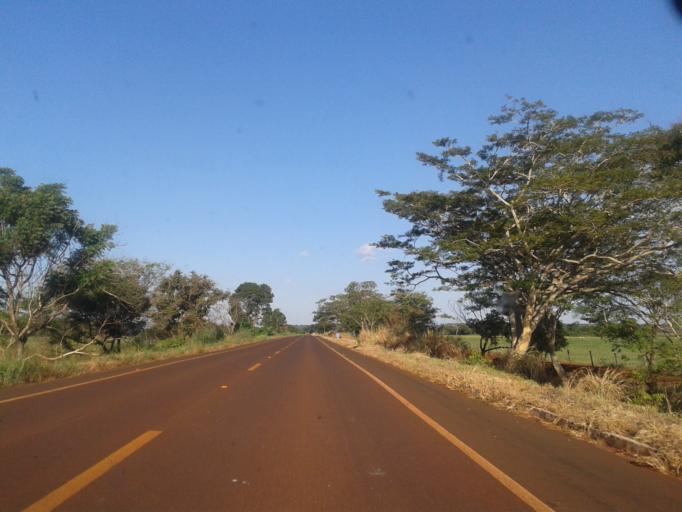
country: BR
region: Minas Gerais
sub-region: Capinopolis
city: Capinopolis
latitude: -18.7093
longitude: -49.8522
